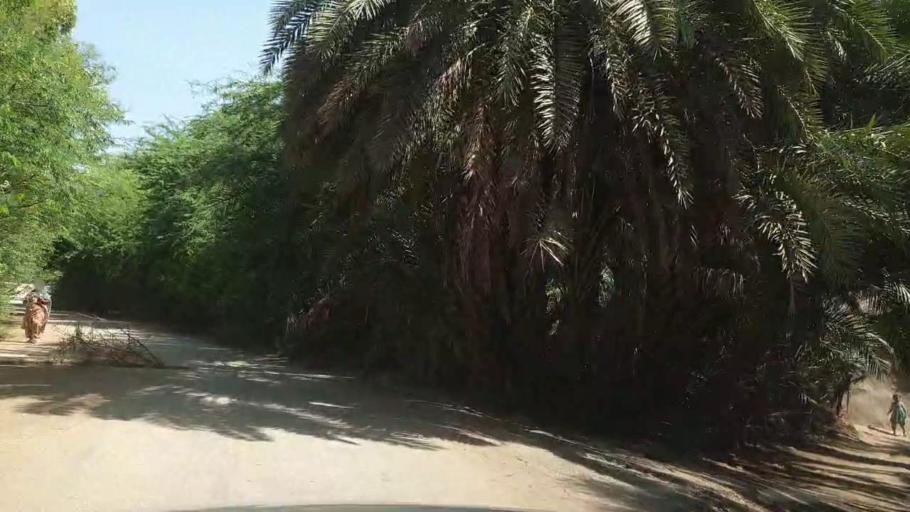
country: PK
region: Sindh
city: Rohri
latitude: 27.6912
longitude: 68.9491
